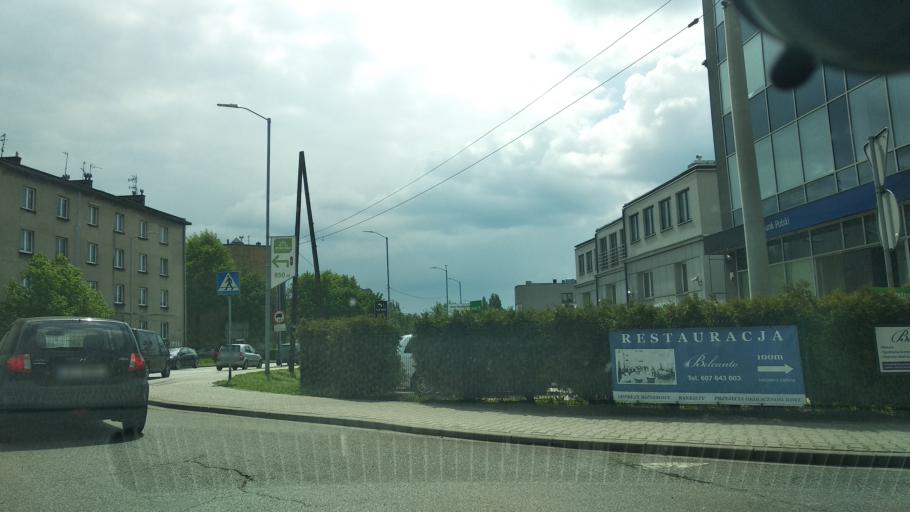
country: PL
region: Silesian Voivodeship
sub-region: Katowice
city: Katowice
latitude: 50.2357
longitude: 18.9781
